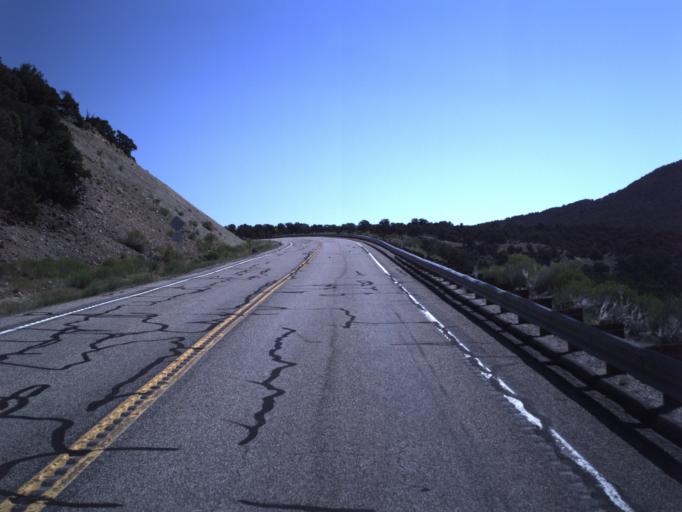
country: US
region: Utah
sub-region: Wayne County
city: Loa
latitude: 38.6903
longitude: -111.3996
